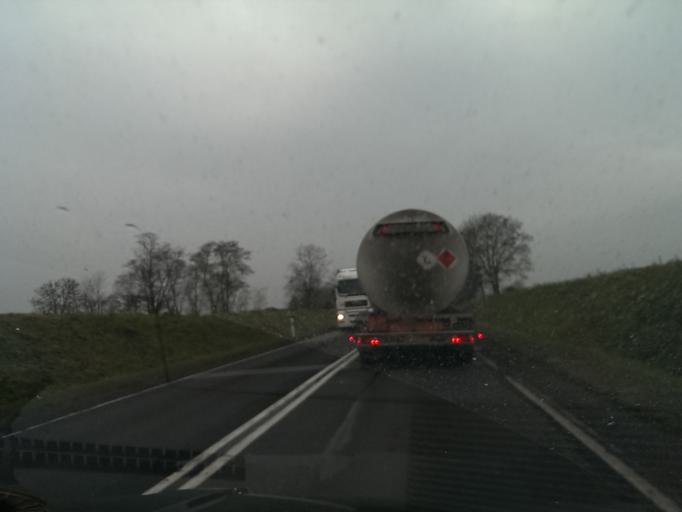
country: PL
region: Kujawsko-Pomorskie
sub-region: Powiat nakielski
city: Slesin
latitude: 53.1683
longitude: 17.6737
